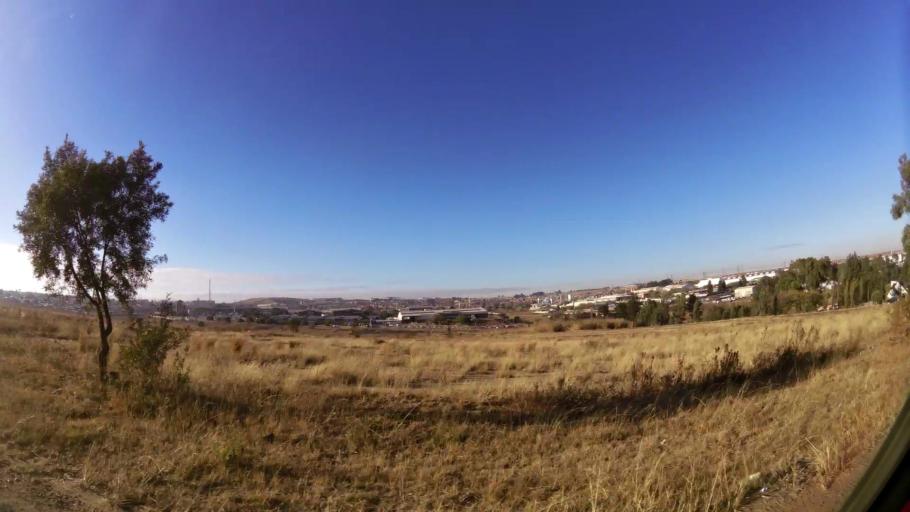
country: ZA
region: Gauteng
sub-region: City of Johannesburg Metropolitan Municipality
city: Midrand
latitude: -26.0308
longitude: 28.1498
